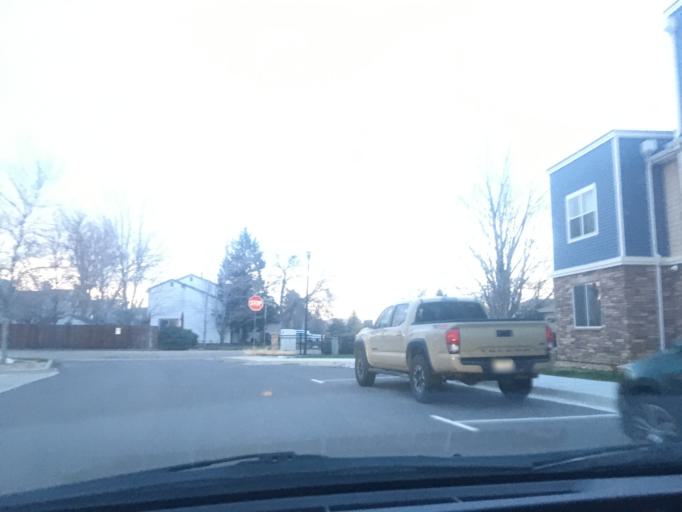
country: US
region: Colorado
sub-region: Boulder County
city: Lafayette
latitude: 39.9734
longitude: -105.0915
